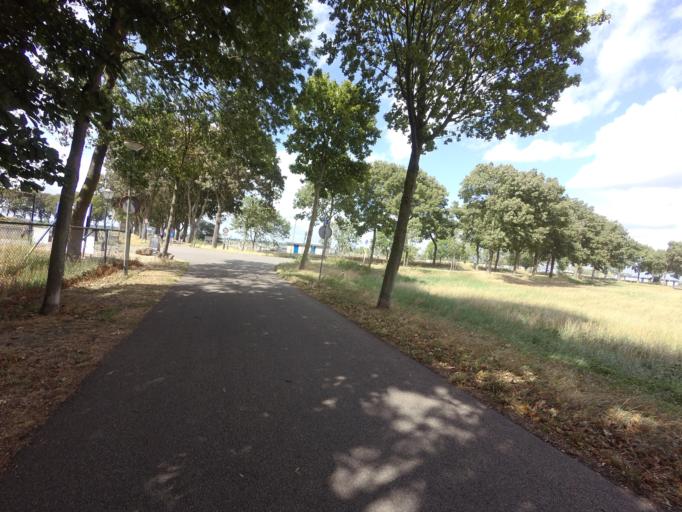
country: NL
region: Limburg
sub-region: Gemeente Maasgouw
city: Maasbracht
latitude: 51.1333
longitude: 5.8484
